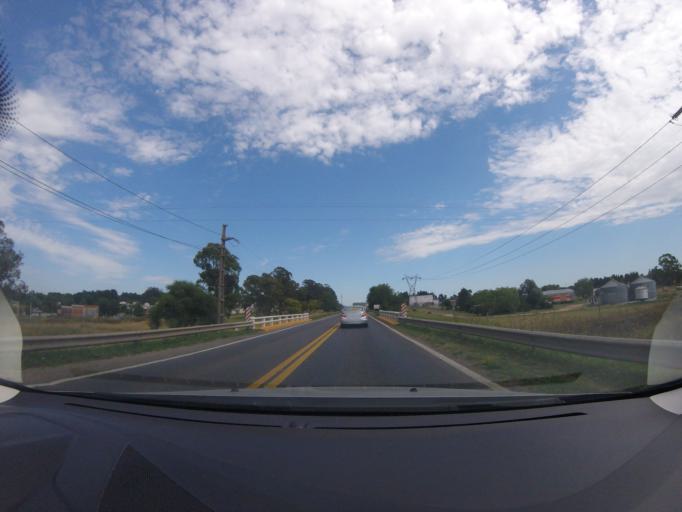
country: AR
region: Buenos Aires
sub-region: Partido de Tandil
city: Tandil
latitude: -37.2932
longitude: -59.1407
